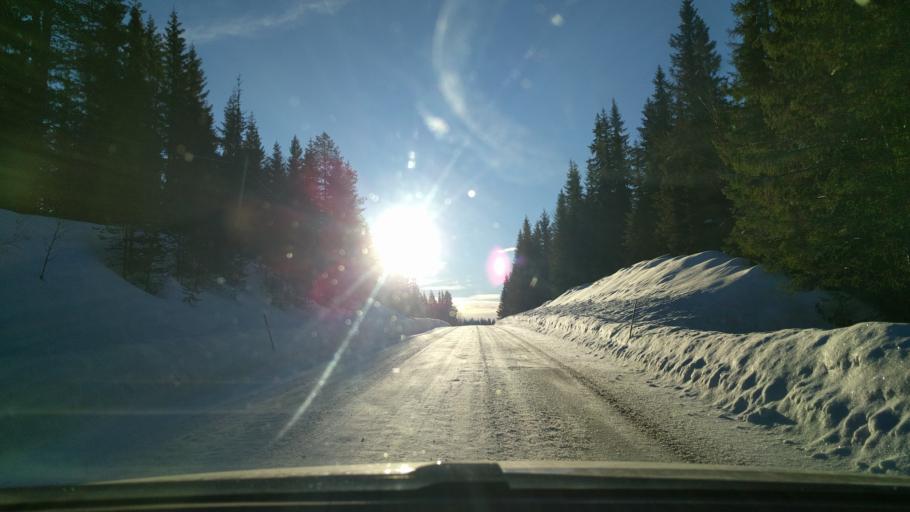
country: NO
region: Hedmark
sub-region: Trysil
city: Innbygda
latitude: 61.1025
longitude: 12.1377
